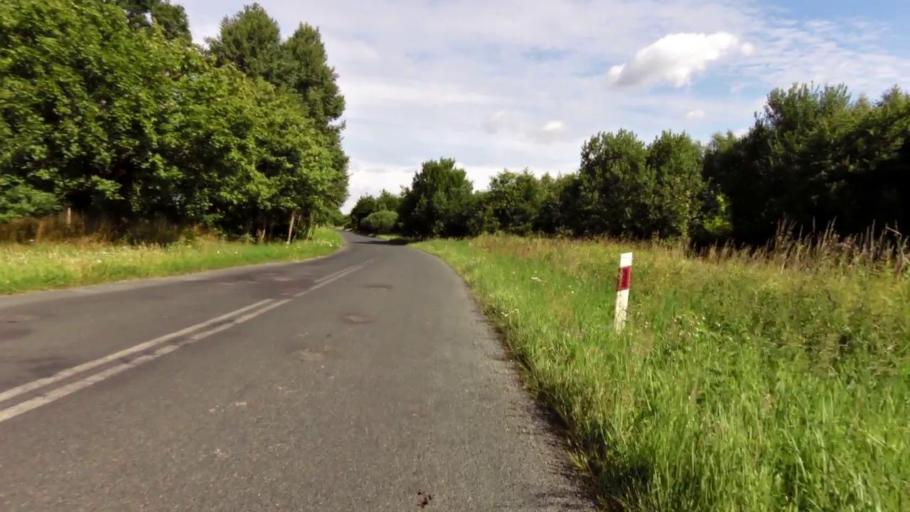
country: PL
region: West Pomeranian Voivodeship
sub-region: Powiat stargardzki
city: Dobrzany
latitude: 53.3890
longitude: 15.4342
